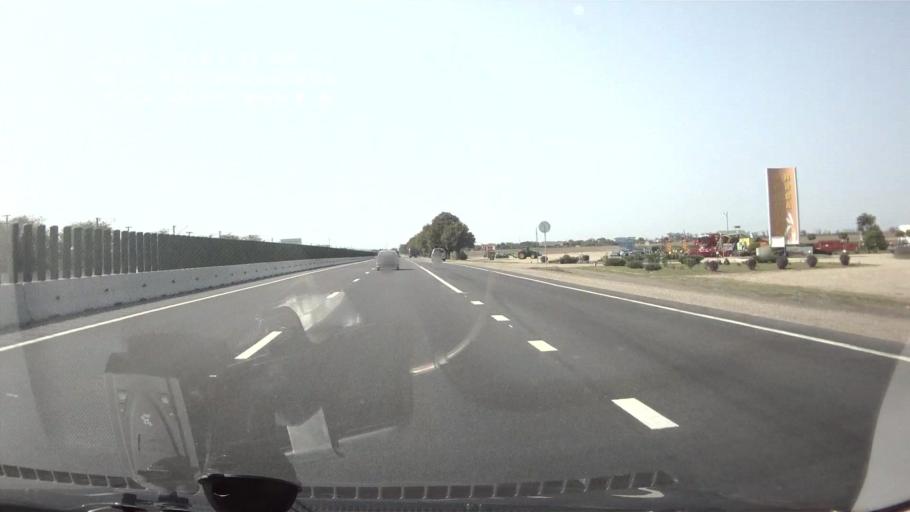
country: RU
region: Adygeya
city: Khatukay
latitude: 45.2198
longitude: 39.6028
